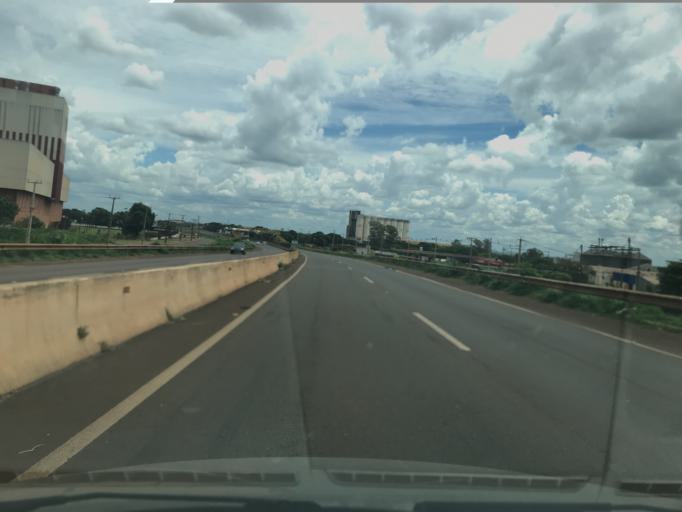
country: BR
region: Parana
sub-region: Paicandu
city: Paicandu
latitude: -23.4464
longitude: -51.9969
